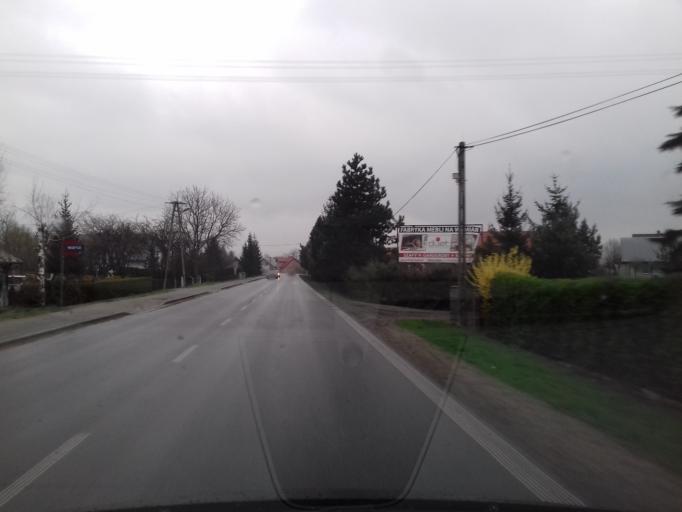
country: PL
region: Lesser Poland Voivodeship
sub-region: Powiat nowosadecki
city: Stary Sacz
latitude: 49.5957
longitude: 20.6340
